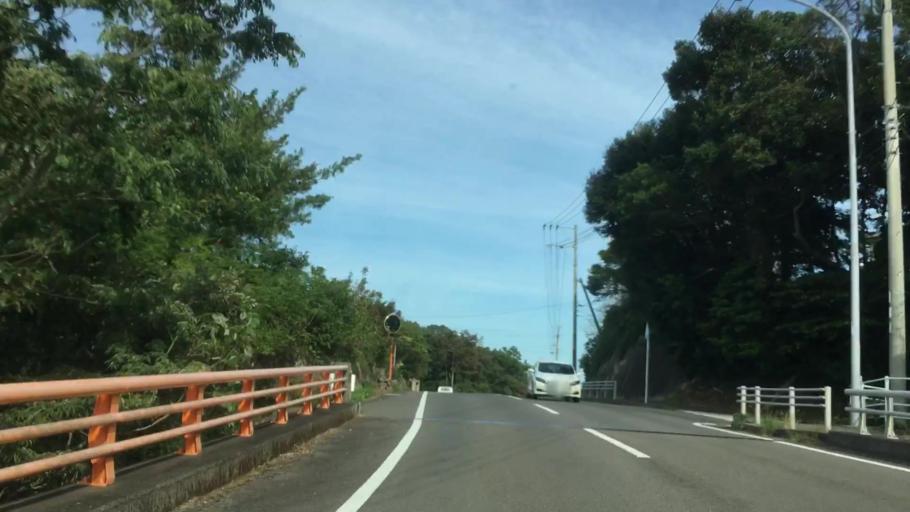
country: JP
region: Nagasaki
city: Sasebo
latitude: 33.0088
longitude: 129.6569
